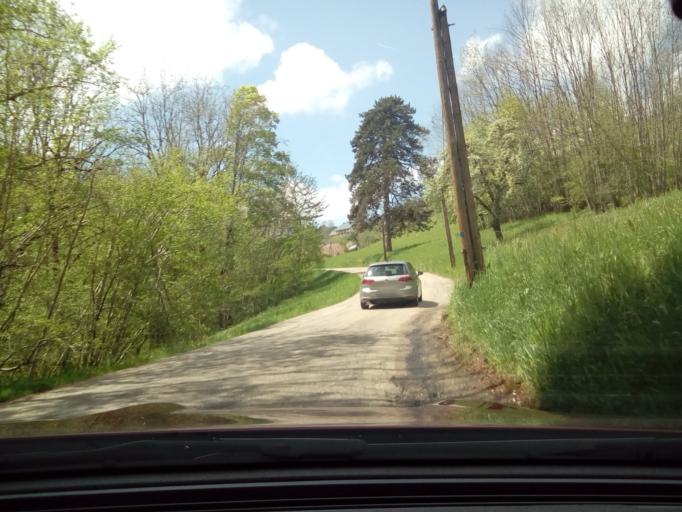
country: FR
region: Rhone-Alpes
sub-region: Departement de la Savoie
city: Barby
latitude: 45.6198
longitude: 6.0071
